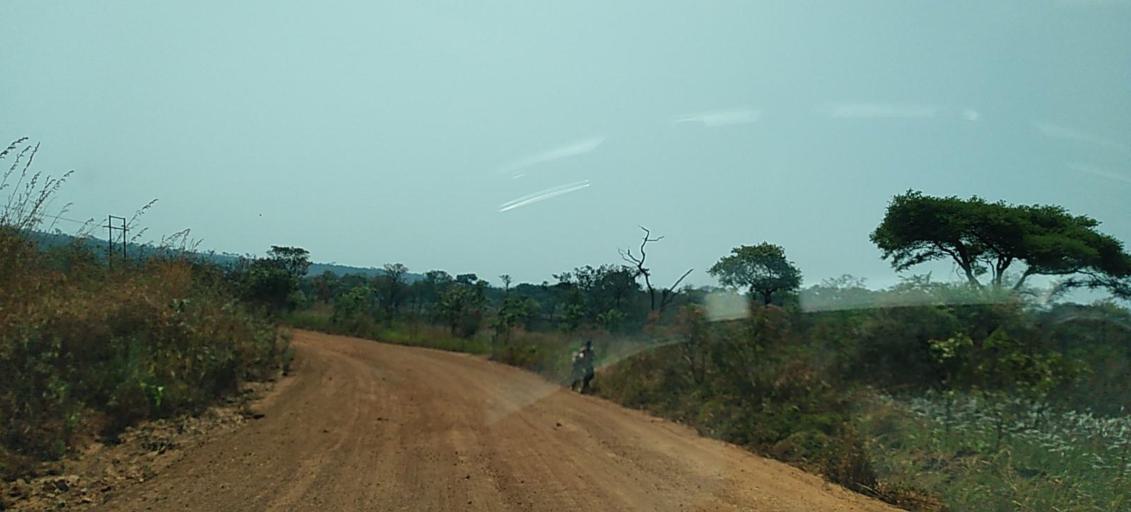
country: ZM
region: North-Western
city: Kansanshi
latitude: -12.0078
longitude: 26.5527
